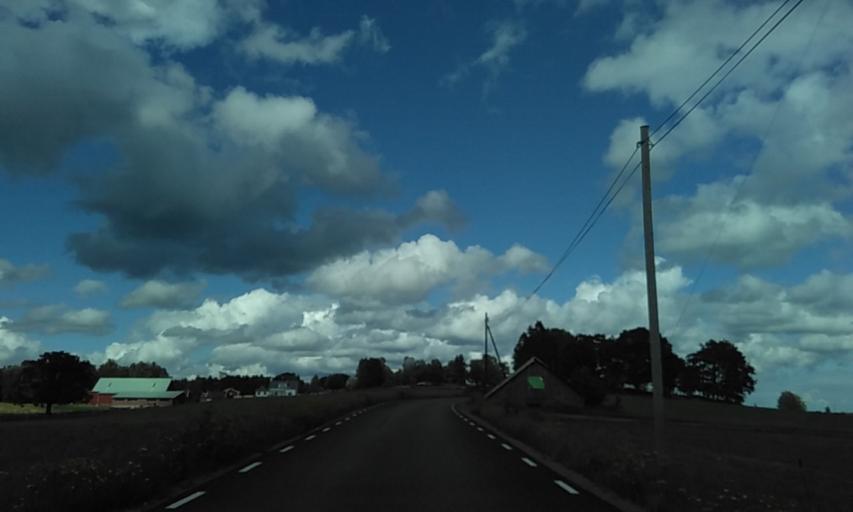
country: SE
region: Vaestra Goetaland
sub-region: Vargarda Kommun
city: Vargarda
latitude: 57.9715
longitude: 12.9017
